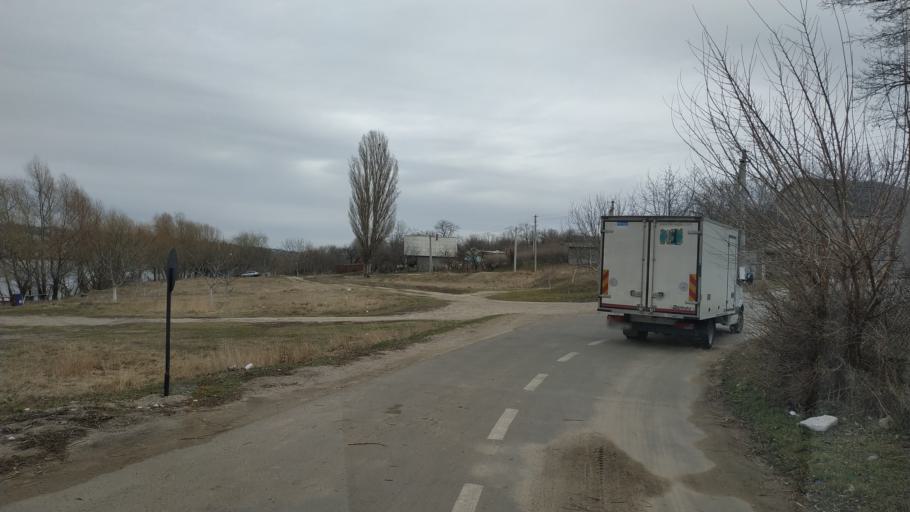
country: MD
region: Telenesti
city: Cocieri
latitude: 47.3499
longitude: 29.0921
